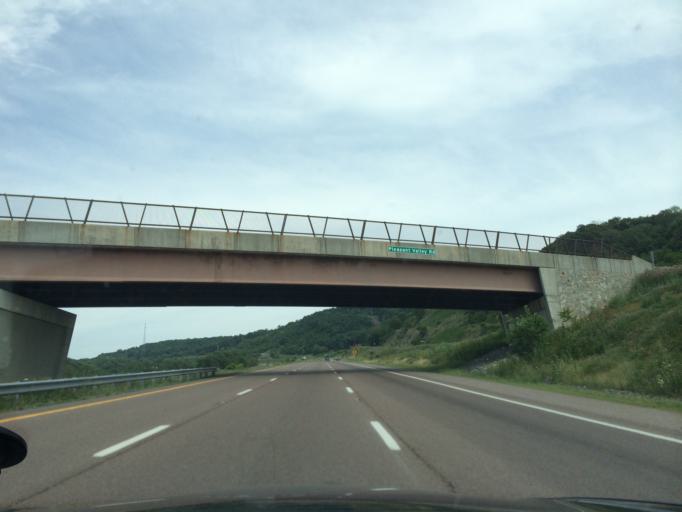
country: US
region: Maryland
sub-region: Allegany County
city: Cumberland
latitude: 39.6940
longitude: -78.6503
